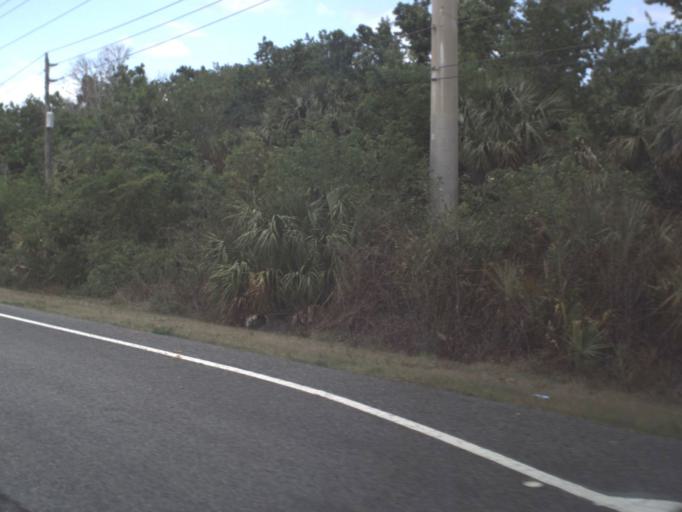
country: US
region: Florida
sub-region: Brevard County
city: Port Saint John
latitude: 28.5282
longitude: -80.8015
